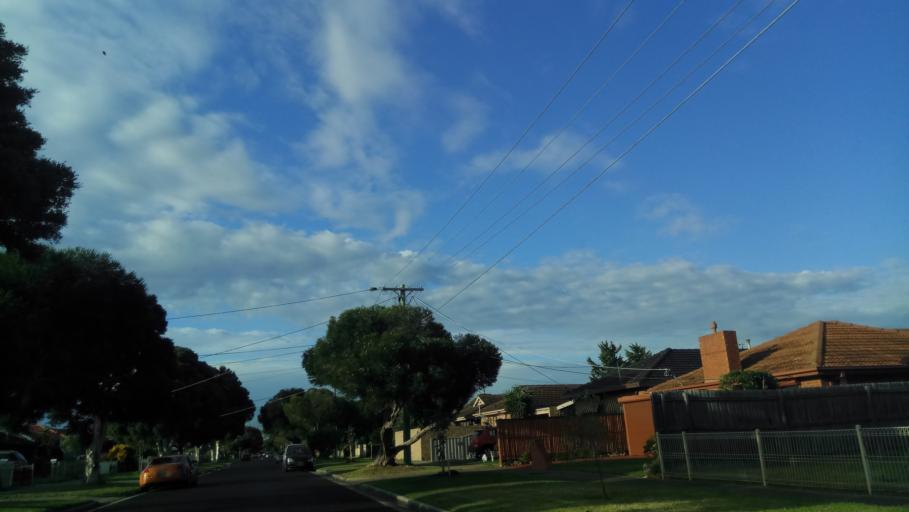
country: AU
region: Victoria
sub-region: Hobsons Bay
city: Laverton
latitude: -37.8676
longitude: 144.7849
